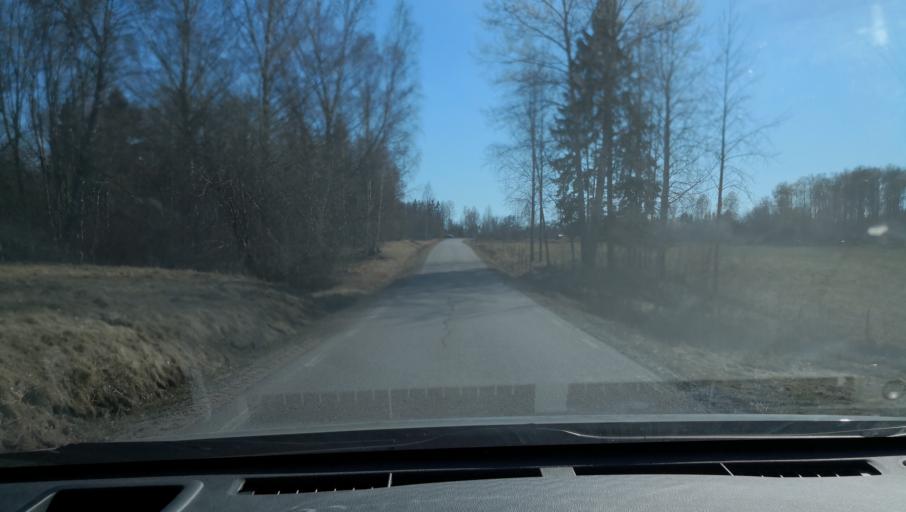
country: SE
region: Dalarna
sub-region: Avesta Kommun
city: Avesta
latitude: 60.0734
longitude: 16.3785
